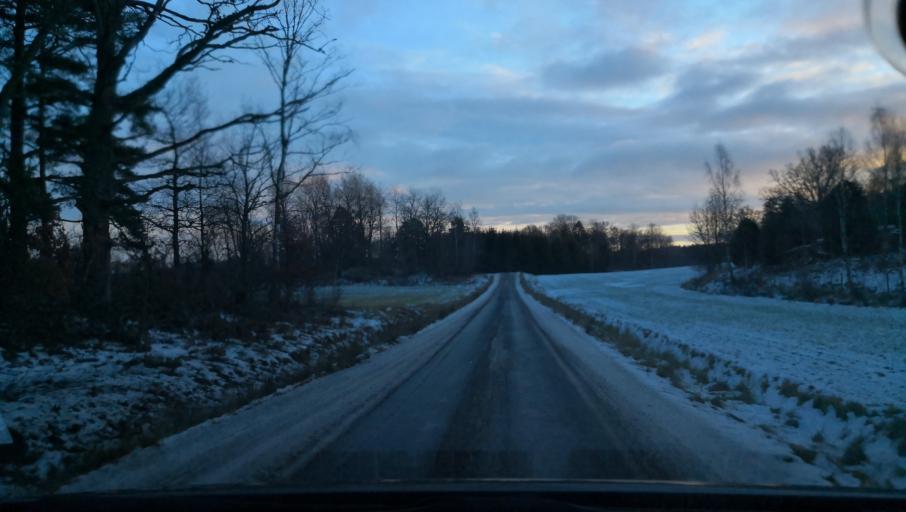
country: SE
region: Soedermanland
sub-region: Flens Kommun
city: Halleforsnas
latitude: 59.2283
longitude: 16.3362
